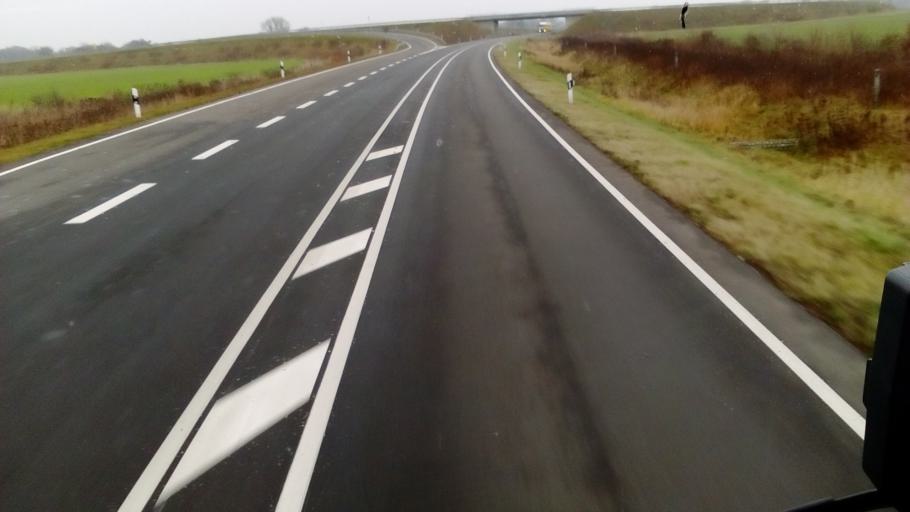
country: DE
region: Brandenburg
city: Pritzwalk
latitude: 53.1433
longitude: 12.2075
